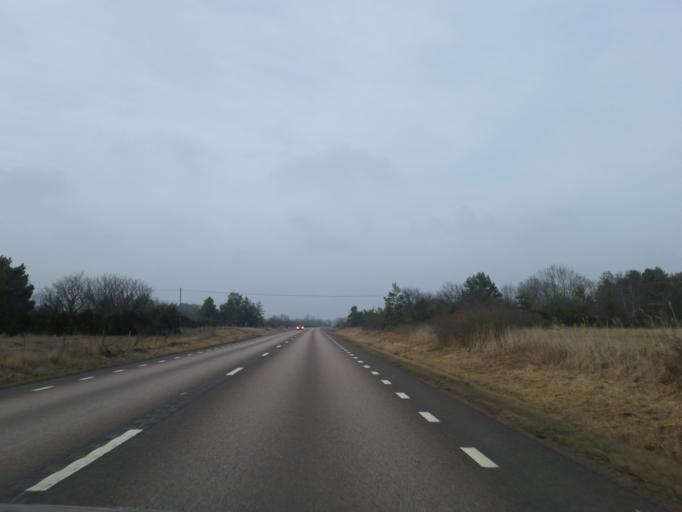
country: SE
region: Kalmar
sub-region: Borgholms Kommun
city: Borgholm
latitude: 57.0872
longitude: 16.9228
